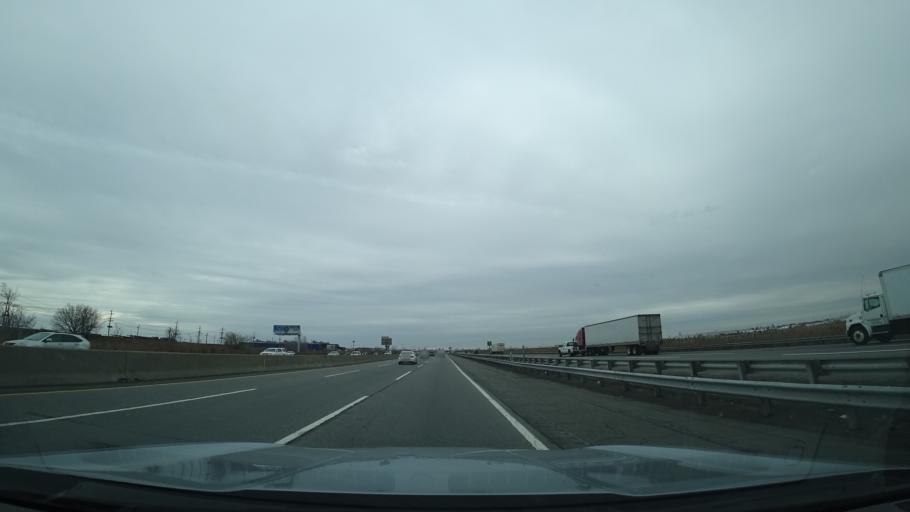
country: US
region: New Jersey
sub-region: Union County
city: Elizabeth
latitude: 40.6809
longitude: -74.1688
